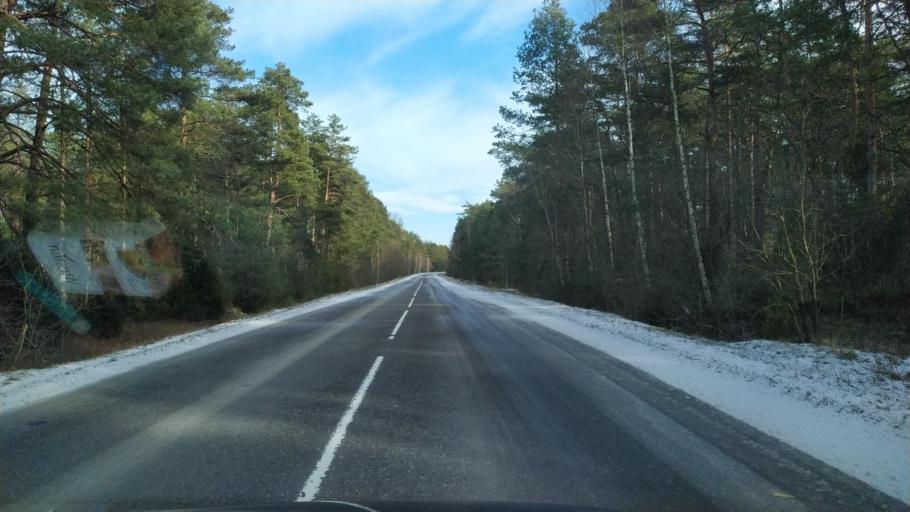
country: BY
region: Brest
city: Pruzhany
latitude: 52.5294
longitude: 24.1807
